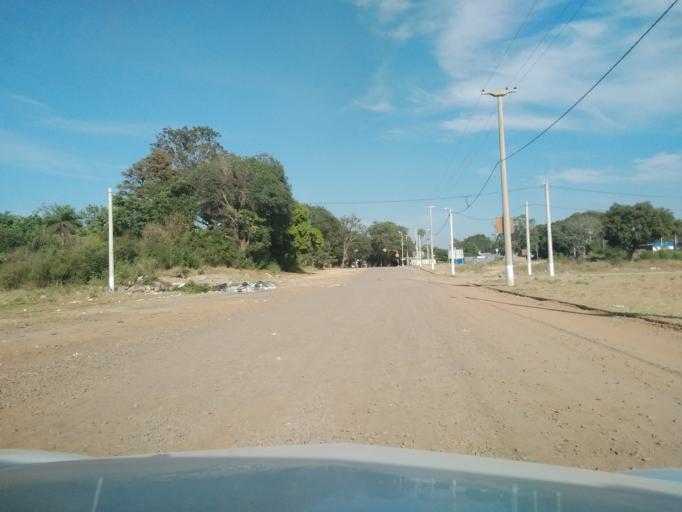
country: AR
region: Corrientes
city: Corrientes
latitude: -27.5077
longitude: -58.8088
